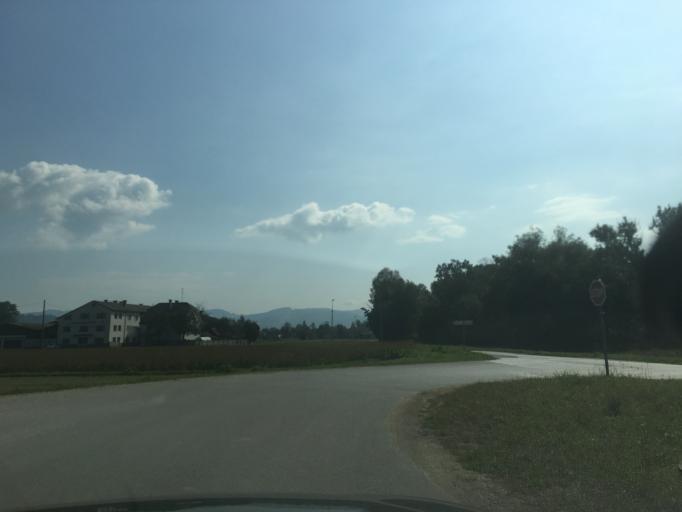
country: SI
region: Dol pri Ljubljani
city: Dol pri Ljubljani
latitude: 46.1045
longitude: 14.5986
